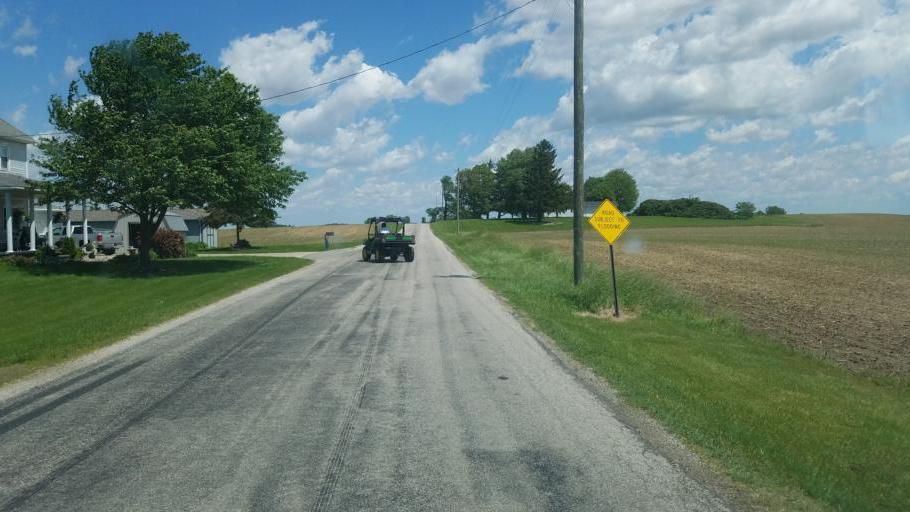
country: US
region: Ohio
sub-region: Richland County
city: Shelby
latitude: 40.8940
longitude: -82.7054
